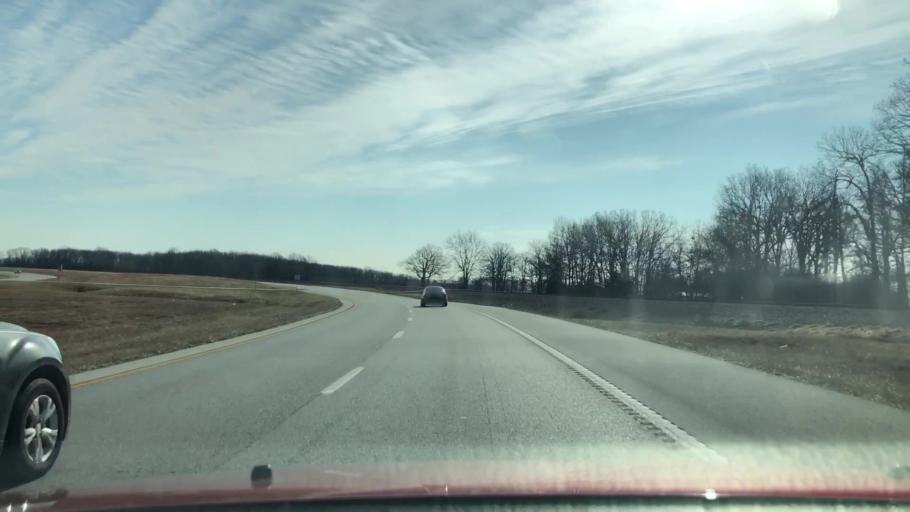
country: US
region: Missouri
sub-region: Webster County
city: Seymour
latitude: 37.1330
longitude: -92.7418
